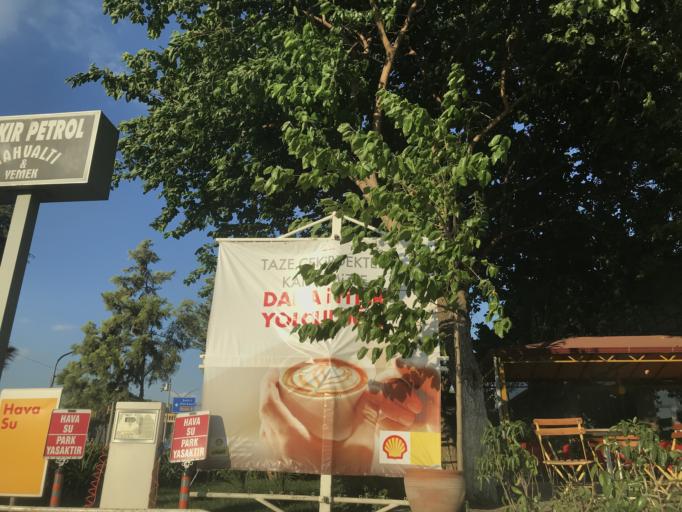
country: TR
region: Aydin
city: Sultanhisar
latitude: 37.8853
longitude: 28.1552
